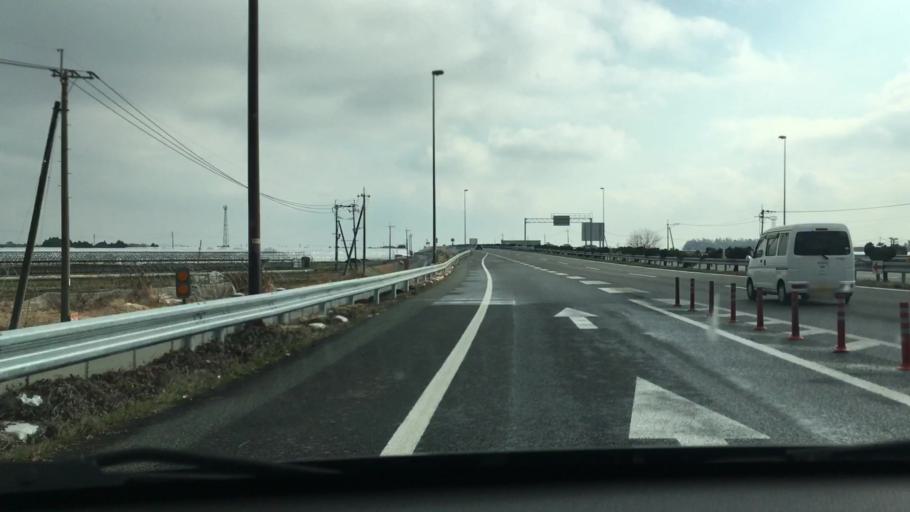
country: JP
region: Kumamoto
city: Ueki
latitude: 32.8928
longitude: 130.7201
